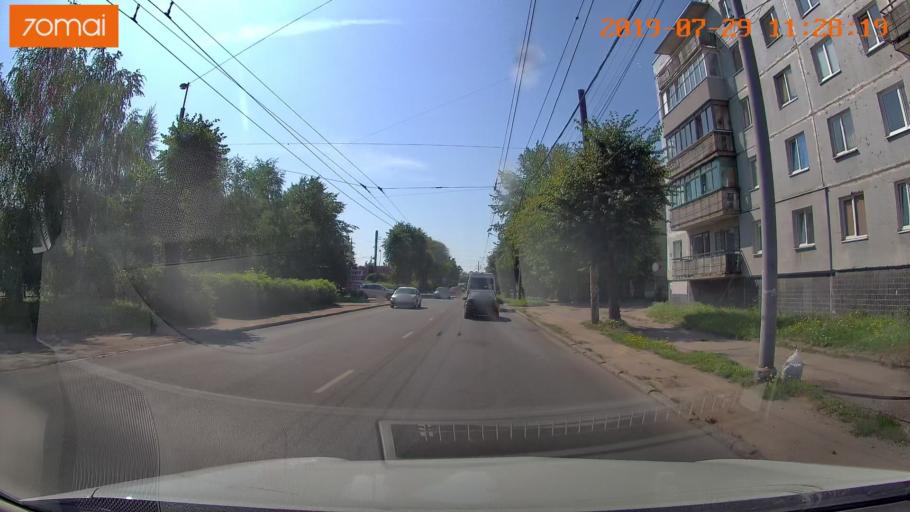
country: RU
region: Kaliningrad
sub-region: Gorod Kaliningrad
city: Kaliningrad
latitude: 54.6875
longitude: 20.5326
